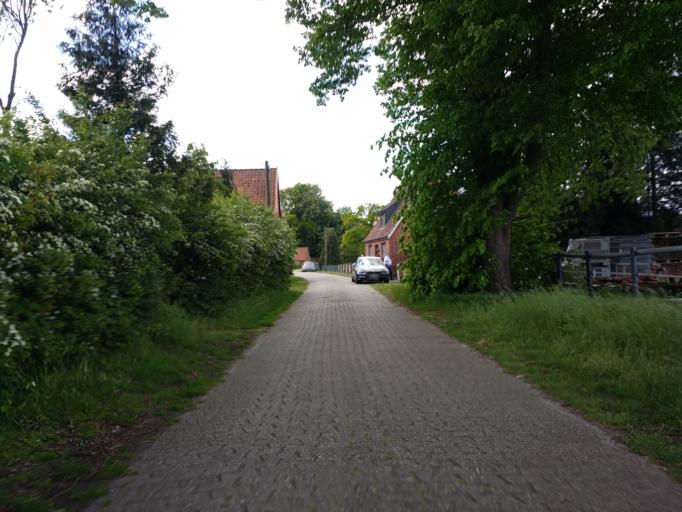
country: DE
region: Lower Saxony
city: Stuhr
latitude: 52.9932
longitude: 8.7574
